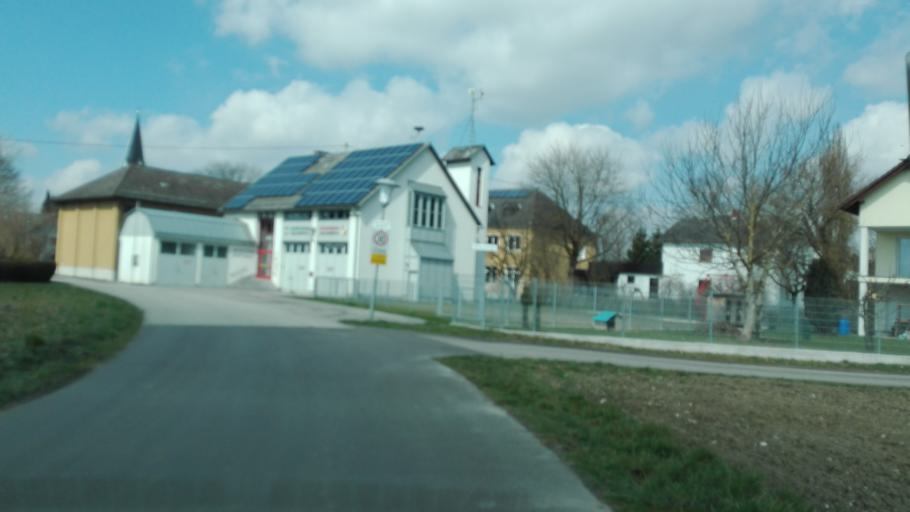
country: AT
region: Upper Austria
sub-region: Politischer Bezirk Urfahr-Umgebung
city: Goldworth
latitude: 48.3261
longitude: 14.1022
